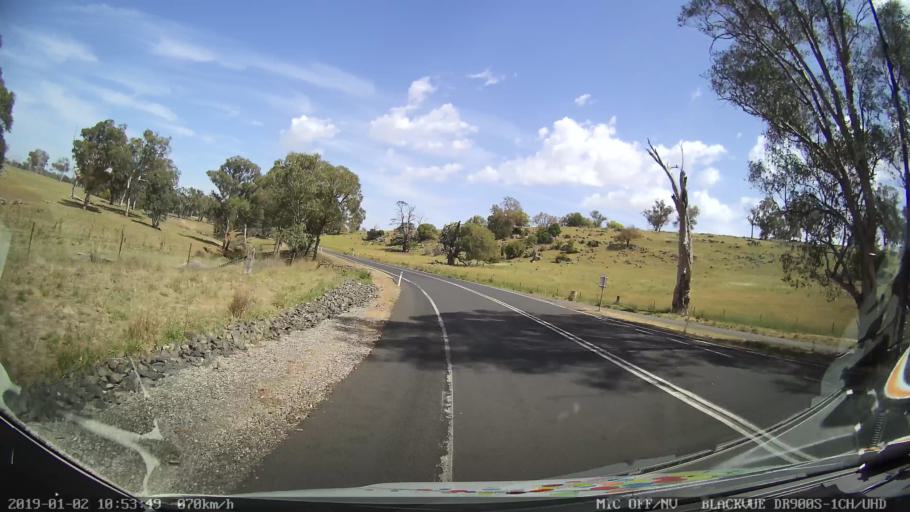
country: AU
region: New South Wales
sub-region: Cootamundra
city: Cootamundra
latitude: -34.6745
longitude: 148.2776
